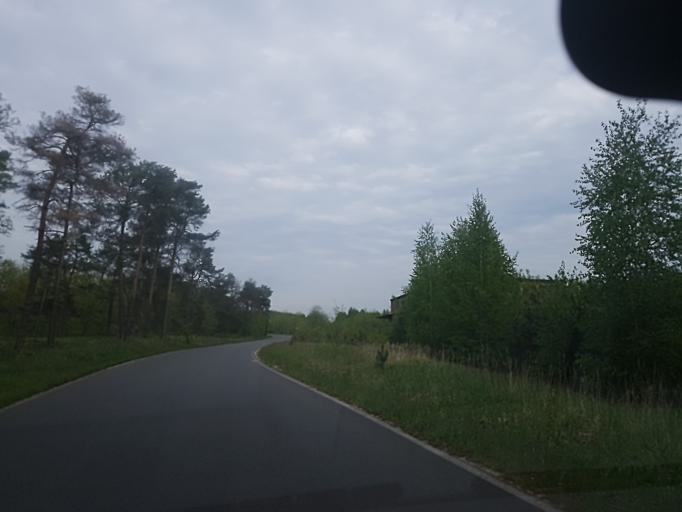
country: DE
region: Brandenburg
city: Finsterwalde
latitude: 51.6024
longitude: 13.7455
